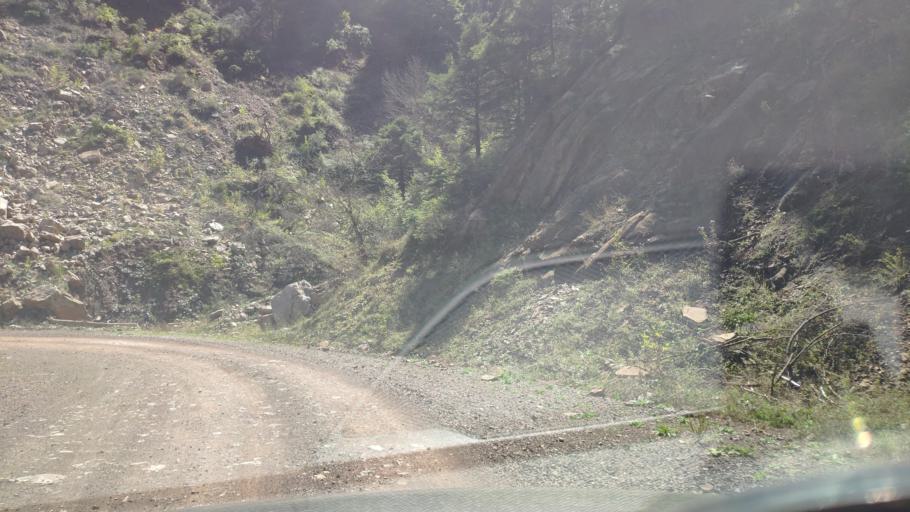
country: GR
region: Central Greece
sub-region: Nomos Evrytanias
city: Kerasochori
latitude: 39.1130
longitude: 21.6225
